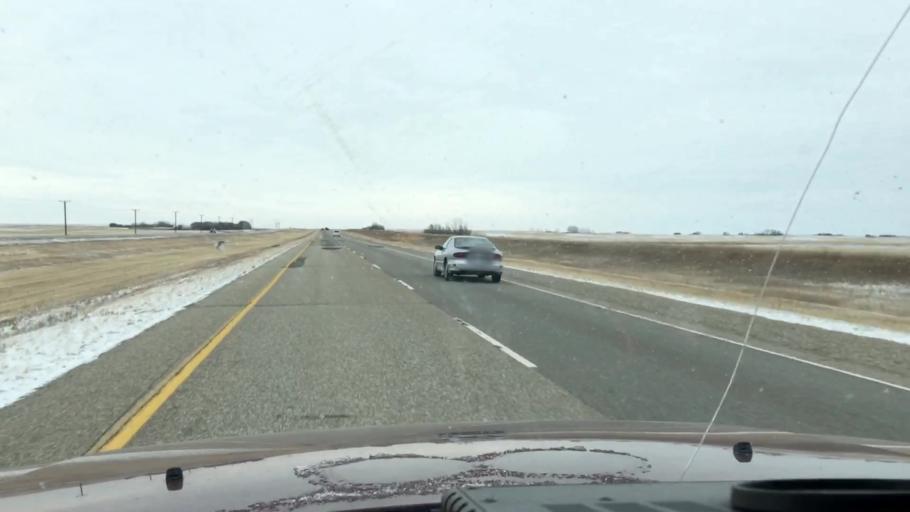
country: CA
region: Saskatchewan
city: Watrous
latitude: 51.4270
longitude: -106.1978
